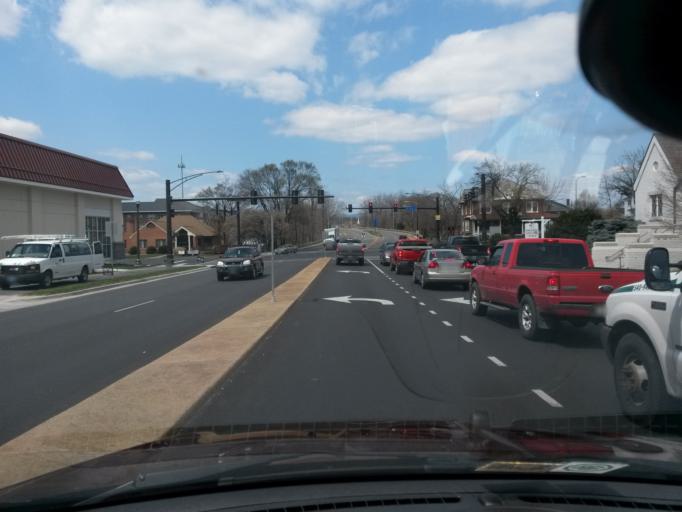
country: US
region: Virginia
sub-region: City of Harrisonburg
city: Harrisonburg
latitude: 38.4421
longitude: -78.8724
